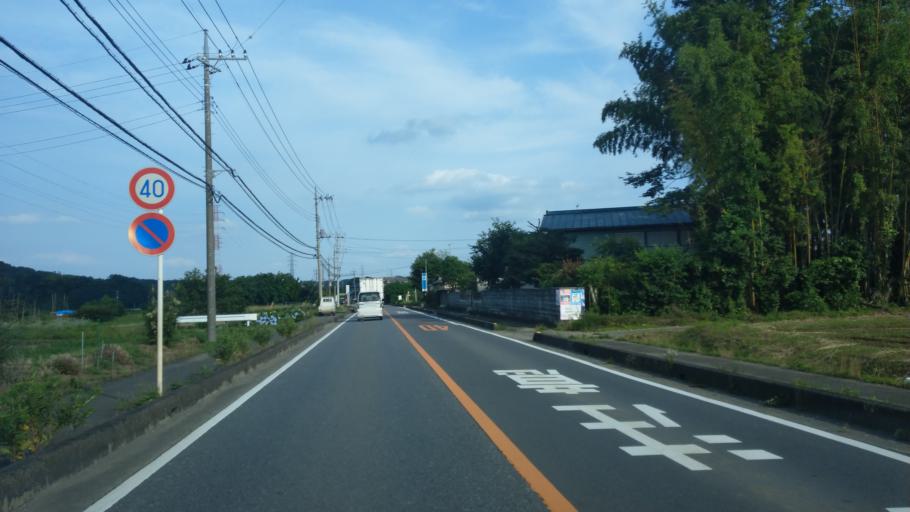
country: JP
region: Saitama
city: Ogawa
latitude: 36.0936
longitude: 139.2761
